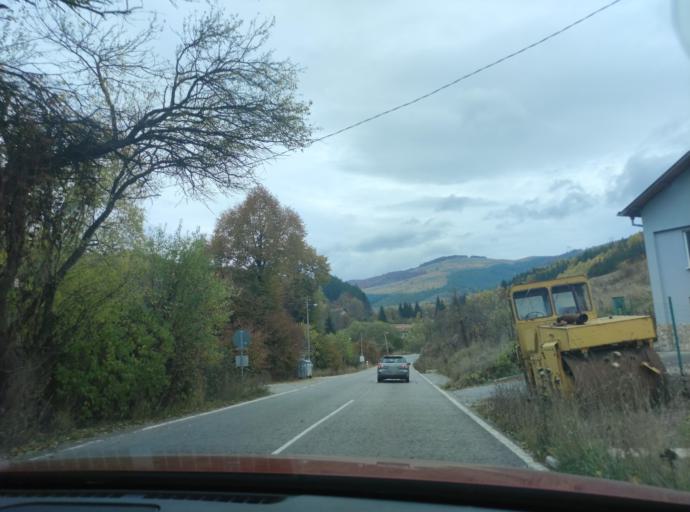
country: BG
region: Sofiya
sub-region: Obshtina Godech
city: Godech
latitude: 43.0685
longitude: 23.1078
